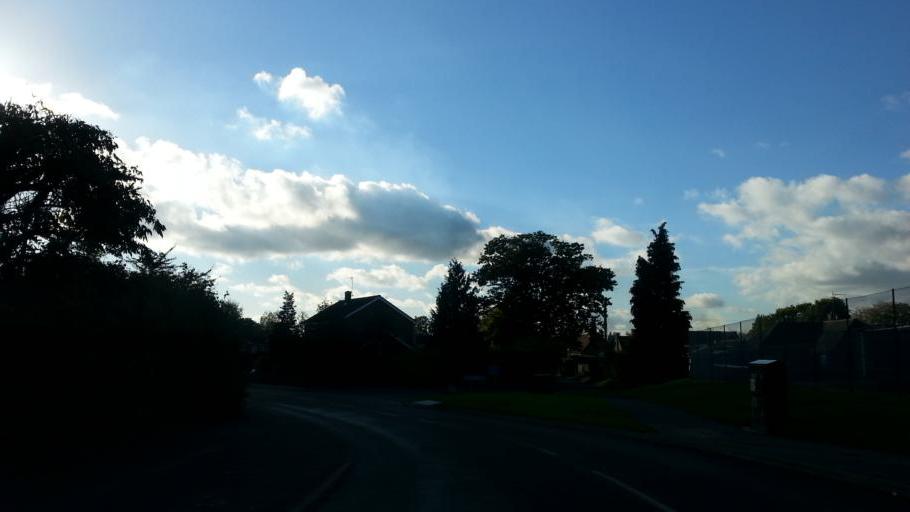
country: GB
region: England
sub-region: Suffolk
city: Thurston
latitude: 52.2534
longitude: 0.8084
